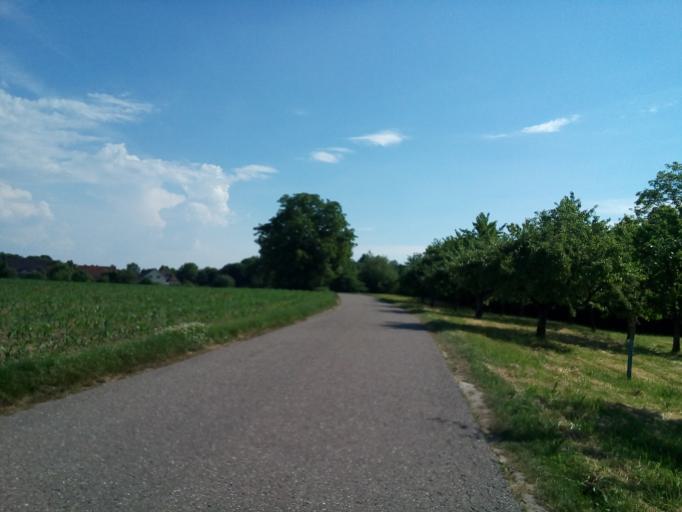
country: DE
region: Baden-Wuerttemberg
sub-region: Karlsruhe Region
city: Lichtenau
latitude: 48.7161
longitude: 8.0014
